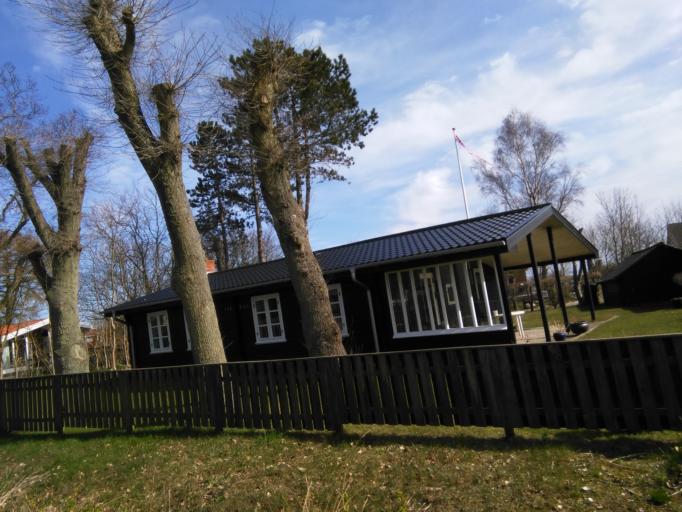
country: DK
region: Central Jutland
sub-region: Arhus Kommune
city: Malling
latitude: 55.9941
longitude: 10.2517
